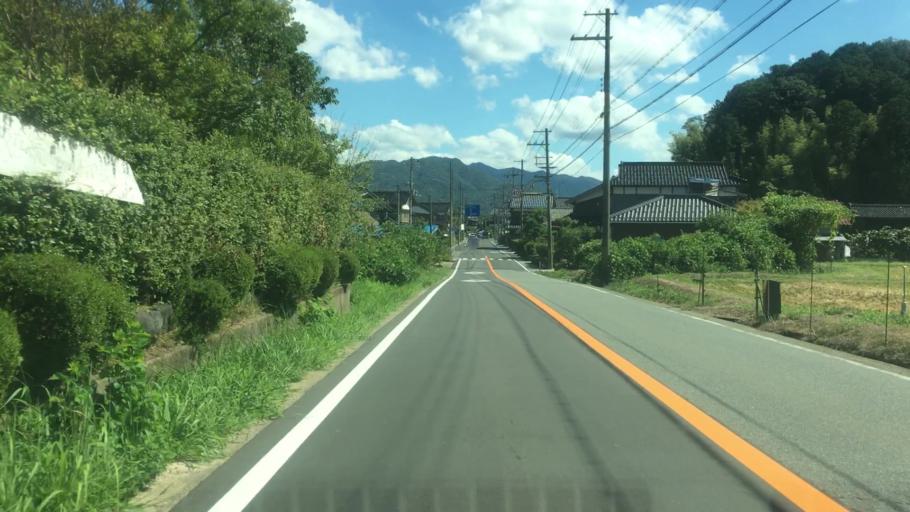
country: JP
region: Hyogo
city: Toyooka
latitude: 35.5908
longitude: 134.9236
